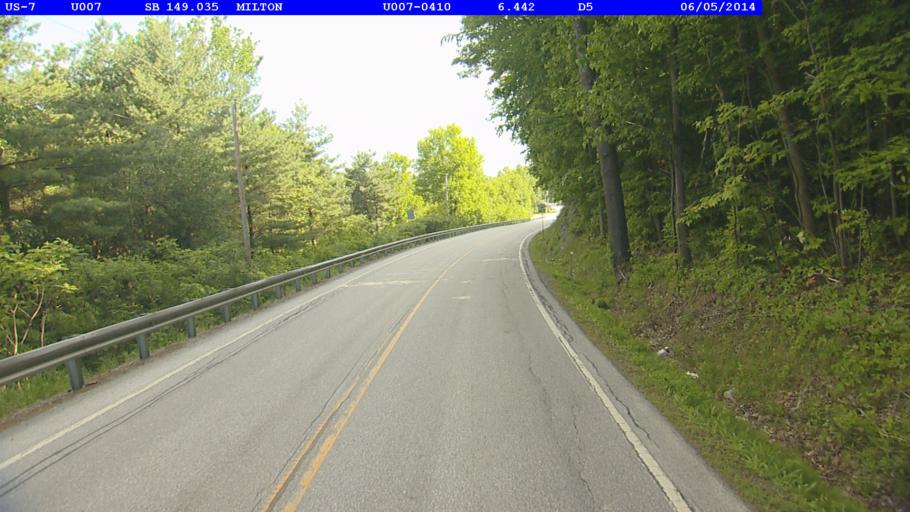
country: US
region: Vermont
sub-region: Chittenden County
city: Milton
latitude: 44.6593
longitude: -73.1122
